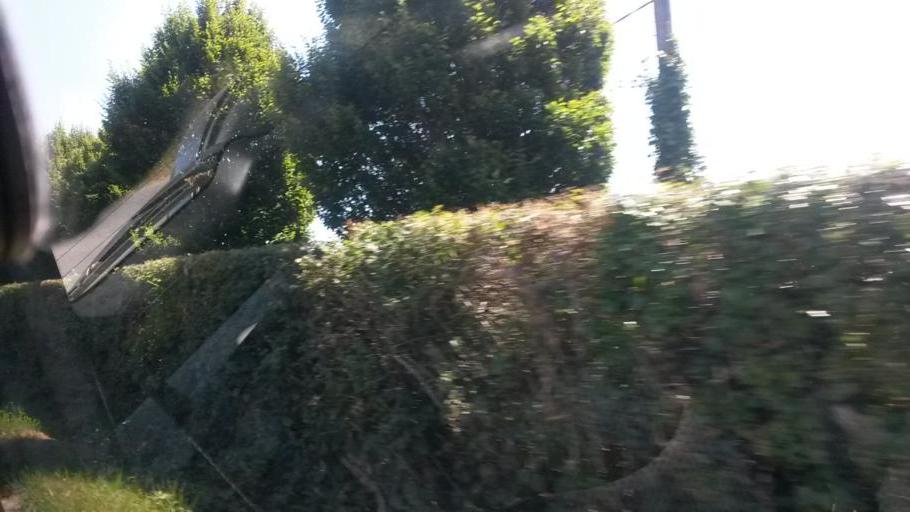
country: IE
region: Leinster
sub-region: Fingal County
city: Swords
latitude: 53.5232
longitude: -6.2883
